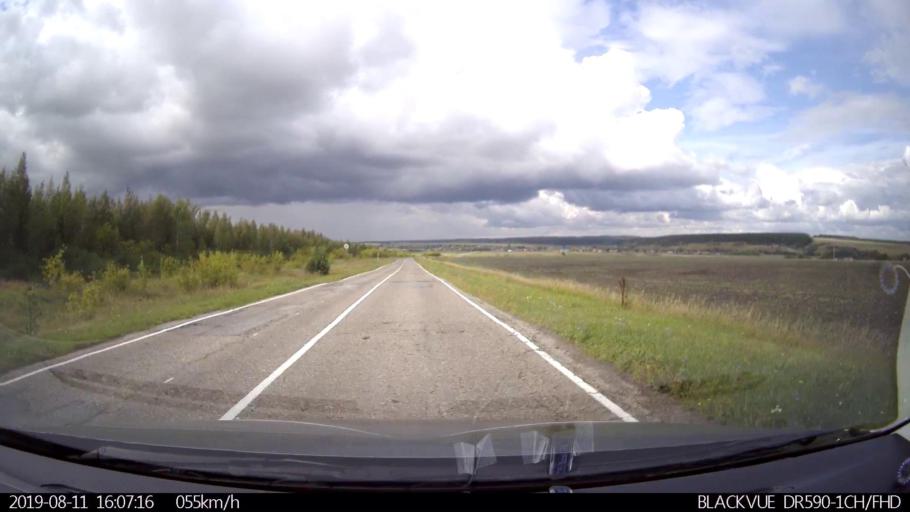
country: RU
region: Ulyanovsk
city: Ignatovka
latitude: 53.9748
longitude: 47.6503
